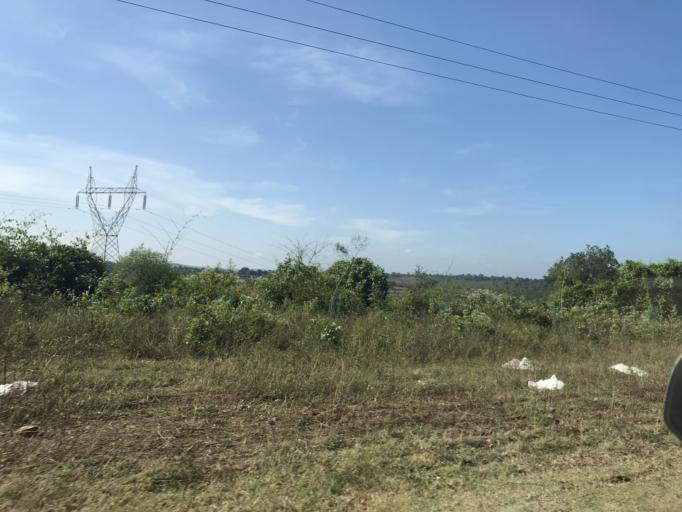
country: IN
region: Karnataka
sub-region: Mysore
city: Heggadadevankote
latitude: 12.0160
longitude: 76.2660
